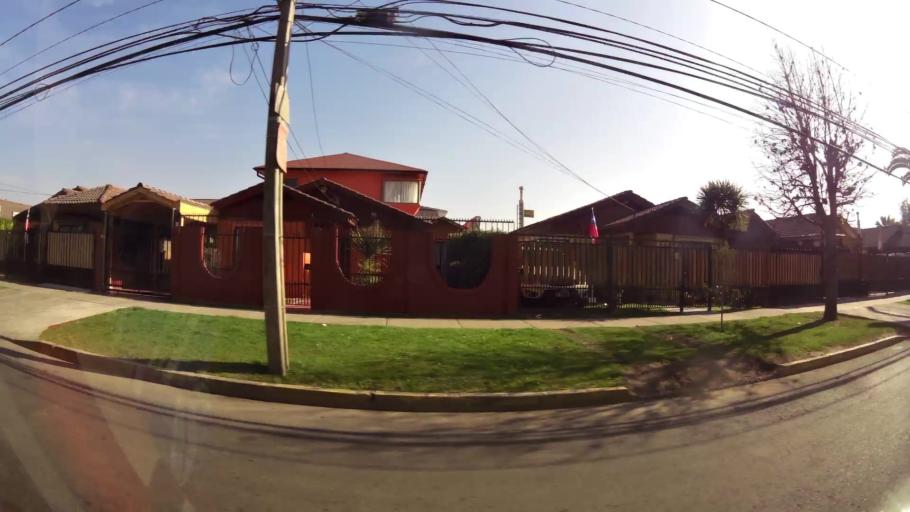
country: CL
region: Santiago Metropolitan
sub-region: Provincia de Santiago
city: Lo Prado
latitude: -33.4540
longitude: -70.7667
